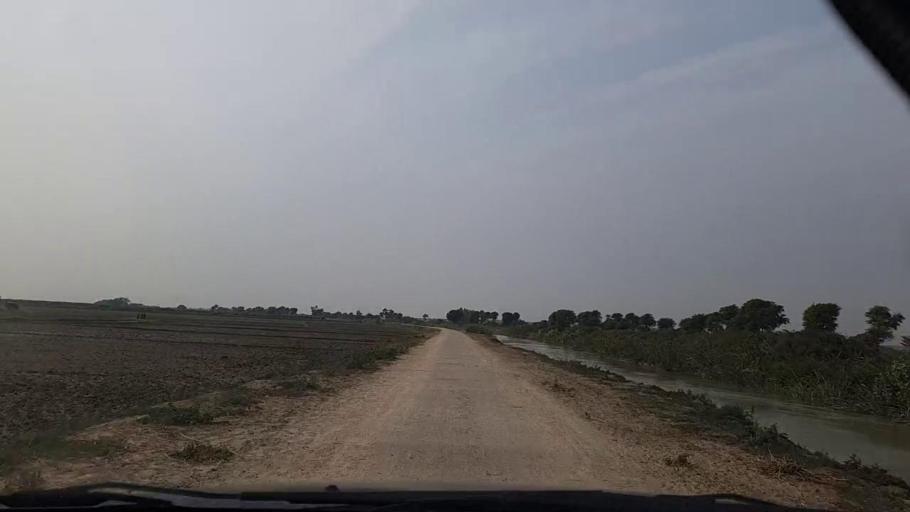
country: PK
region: Sindh
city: Thatta
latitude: 24.5779
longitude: 67.8875
